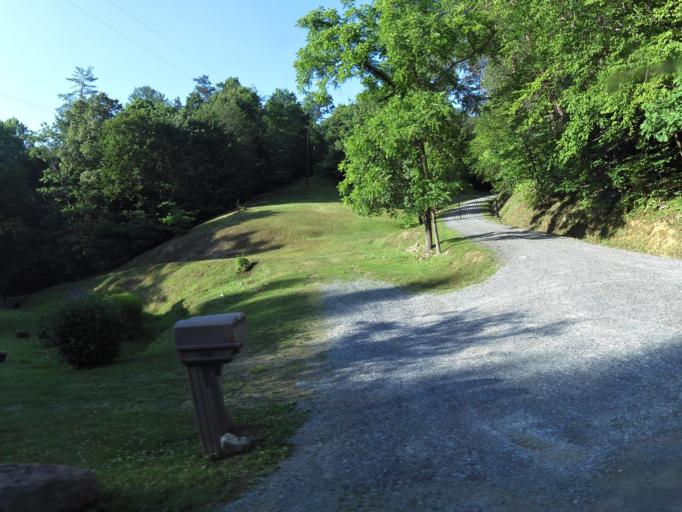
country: US
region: Tennessee
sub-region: Sevier County
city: Pigeon Forge
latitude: 35.8200
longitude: -83.5956
